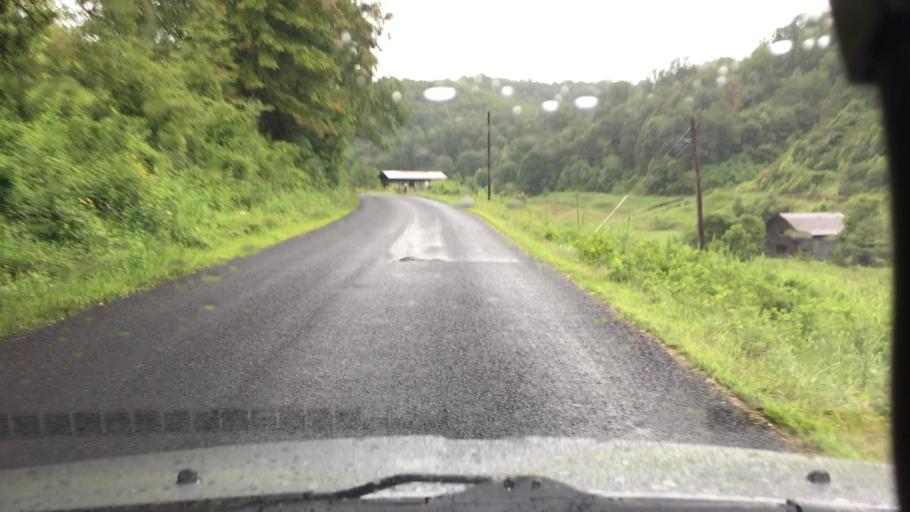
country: US
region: North Carolina
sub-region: Madison County
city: Mars Hill
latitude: 35.9122
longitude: -82.5027
